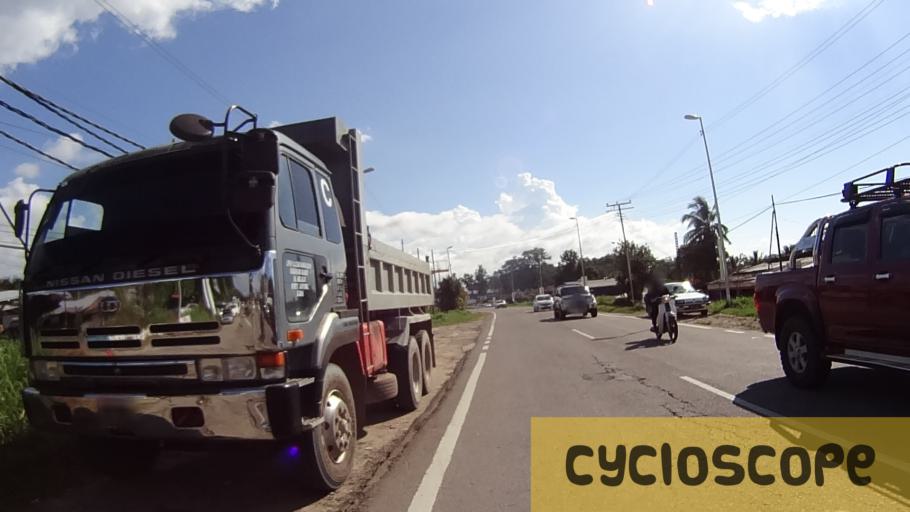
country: MY
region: Sabah
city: Beaufort
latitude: 5.0686
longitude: 115.5506
